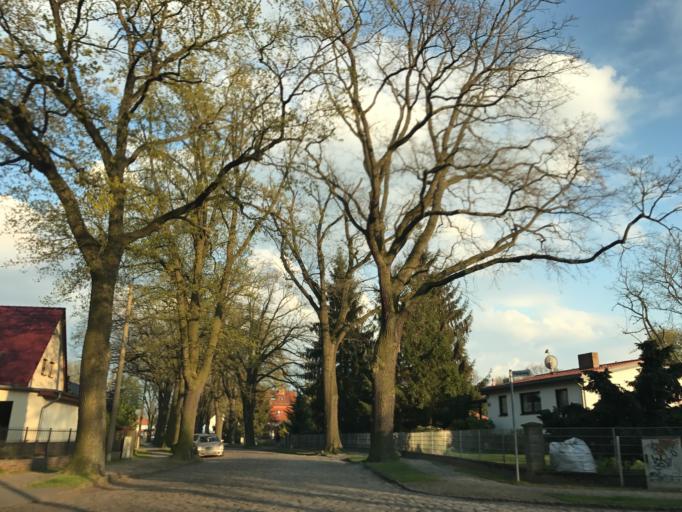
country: DE
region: Brandenburg
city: Dallgow-Doeberitz
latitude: 52.5562
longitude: 13.0664
